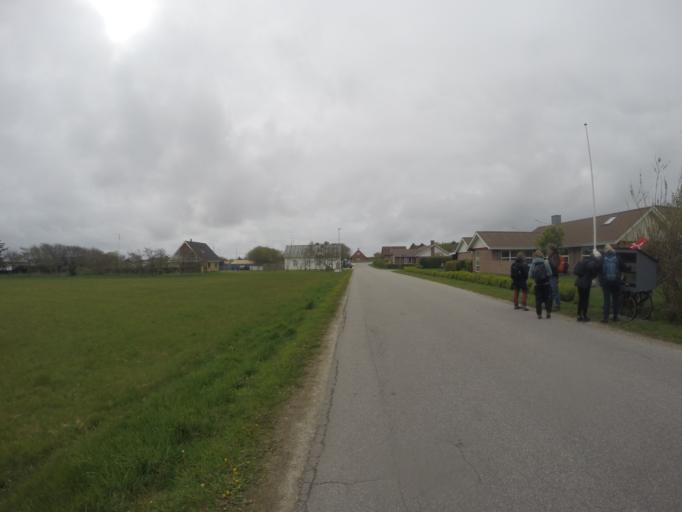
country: DK
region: North Denmark
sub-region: Thisted Kommune
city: Hurup
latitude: 56.9197
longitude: 8.3605
